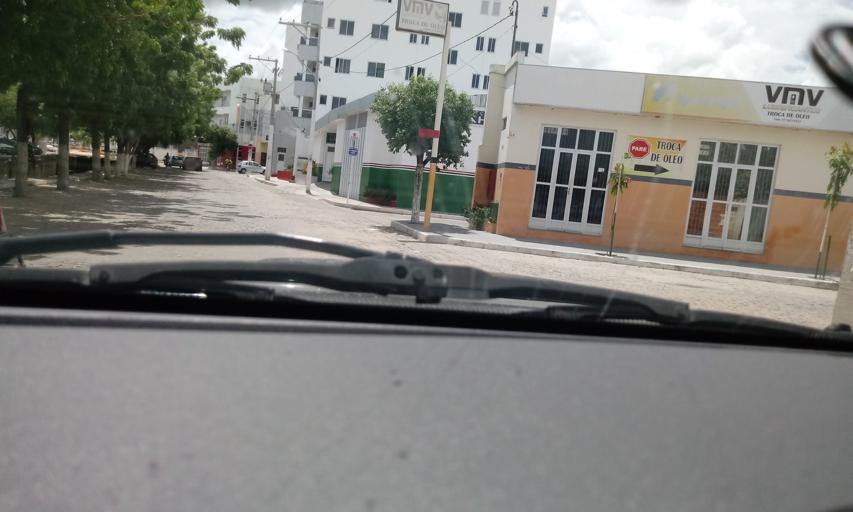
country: BR
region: Bahia
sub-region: Guanambi
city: Guanambi
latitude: -14.2253
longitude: -42.7762
